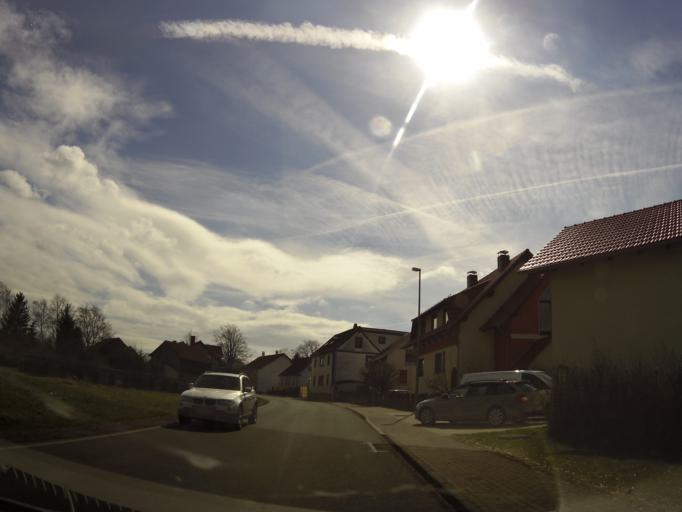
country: DE
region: Thuringia
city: Crawinkel
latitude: 50.7826
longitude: 10.7820
